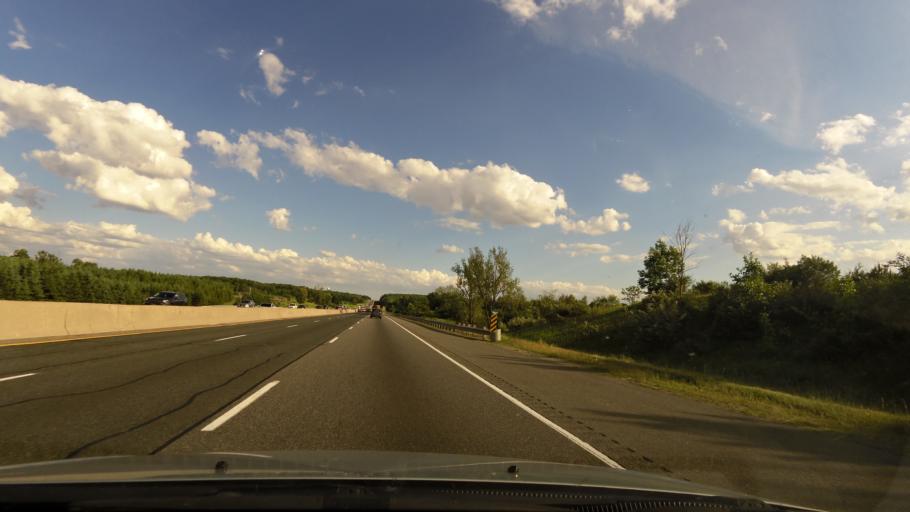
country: CA
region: Ontario
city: Newmarket
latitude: 43.9821
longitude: -79.5808
